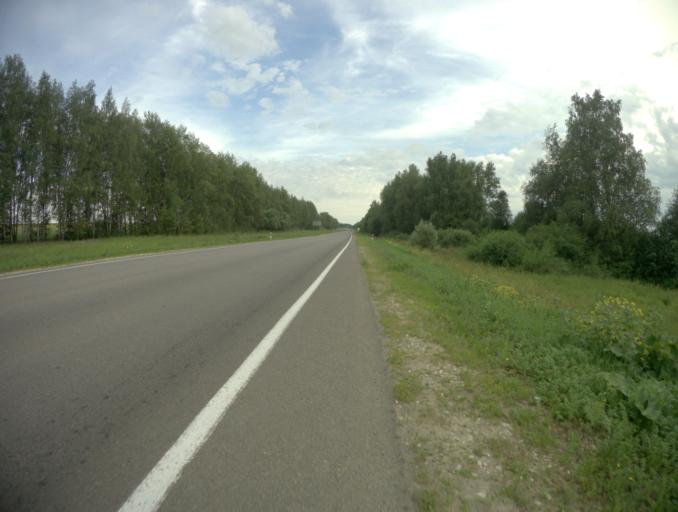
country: RU
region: Vladimir
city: Suzdal'
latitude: 56.3898
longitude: 40.4524
